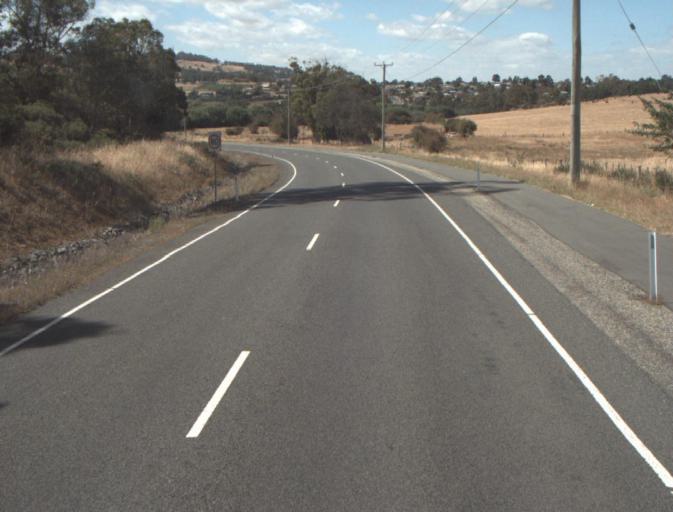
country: AU
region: Tasmania
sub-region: Launceston
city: Newstead
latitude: -41.4235
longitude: 147.1827
